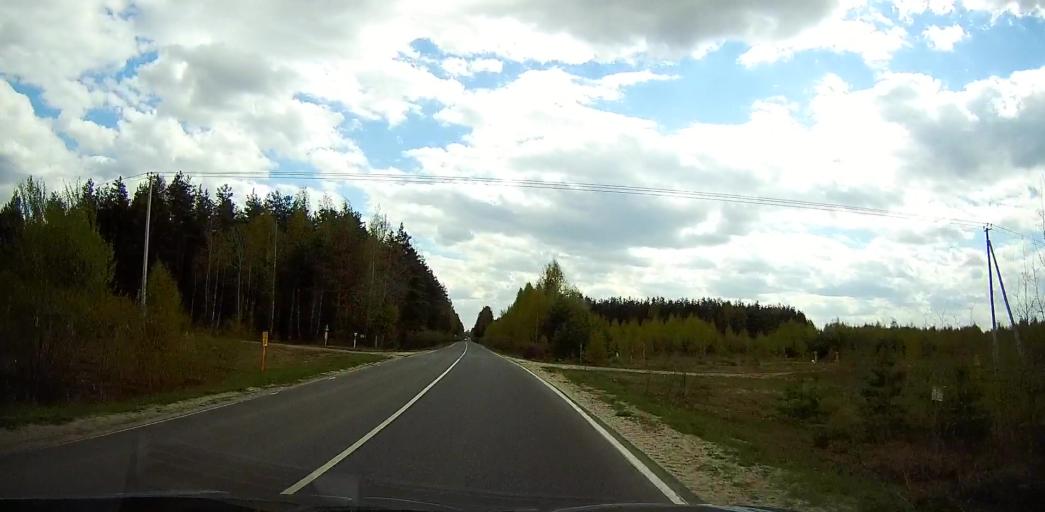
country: RU
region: Moskovskaya
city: Davydovo
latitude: 55.6591
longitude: 38.7540
